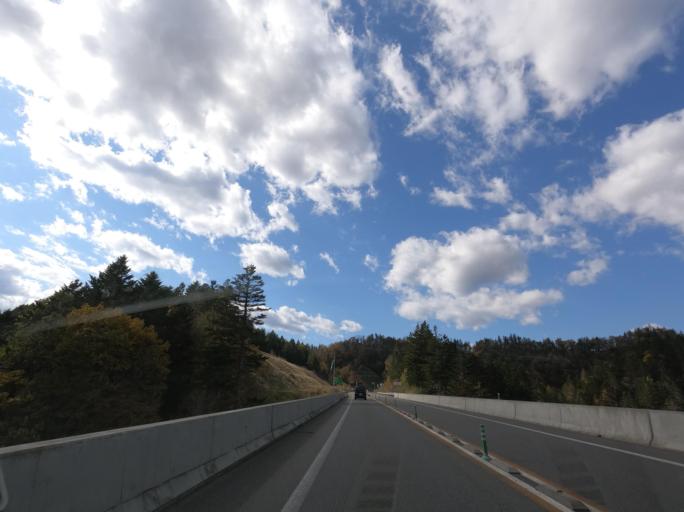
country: JP
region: Hokkaido
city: Kushiro
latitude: 43.0795
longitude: 144.0461
